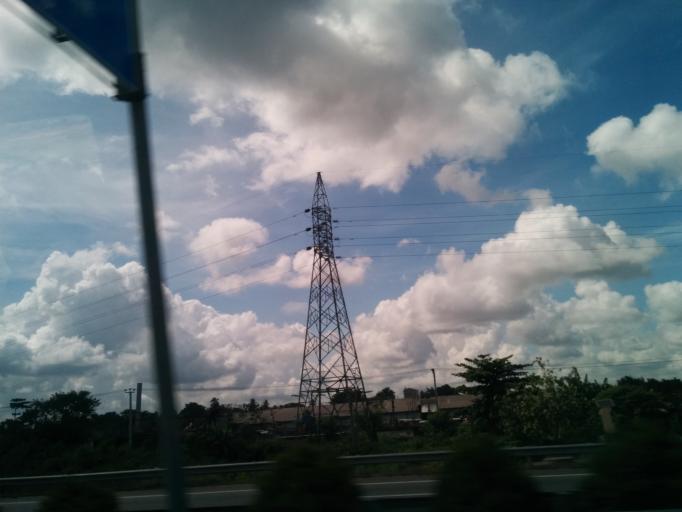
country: LK
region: Western
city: Peliyagoda
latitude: 6.9648
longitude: 79.8909
